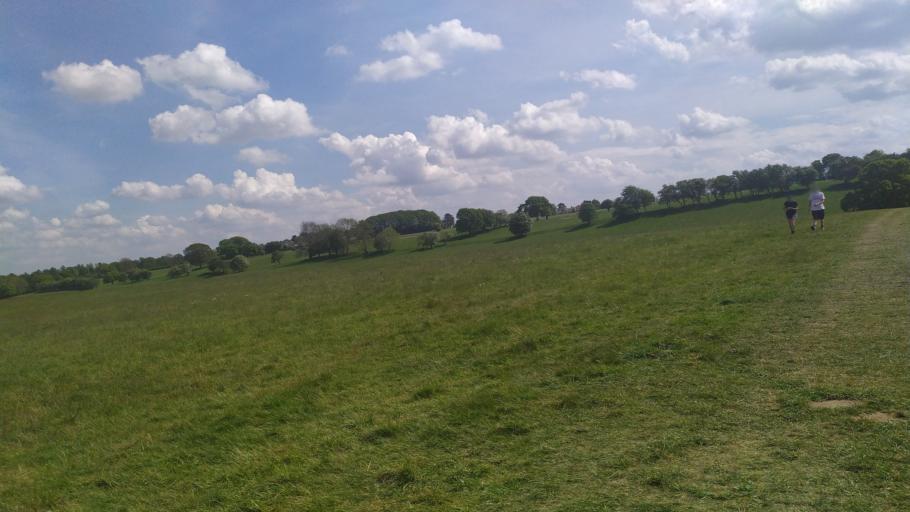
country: GB
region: England
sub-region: City and Borough of Leeds
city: Chapel Allerton
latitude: 53.8677
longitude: -1.5607
